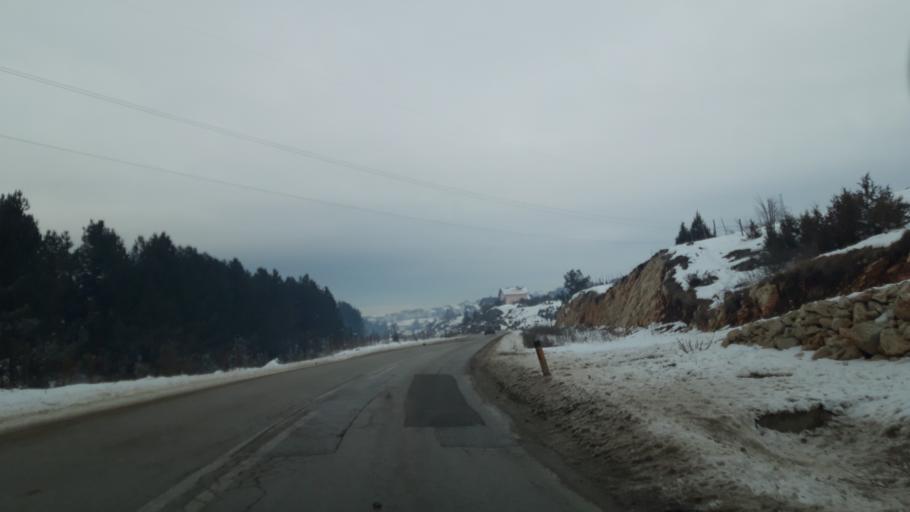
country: BA
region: Republika Srpska
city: Sokolac
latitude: 43.9359
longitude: 18.8147
